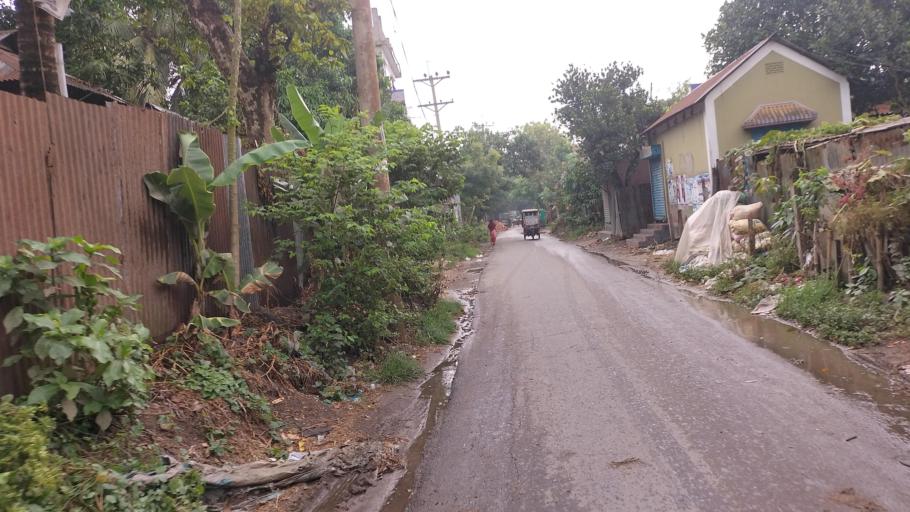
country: BD
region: Dhaka
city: Azimpur
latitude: 23.6747
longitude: 90.3466
